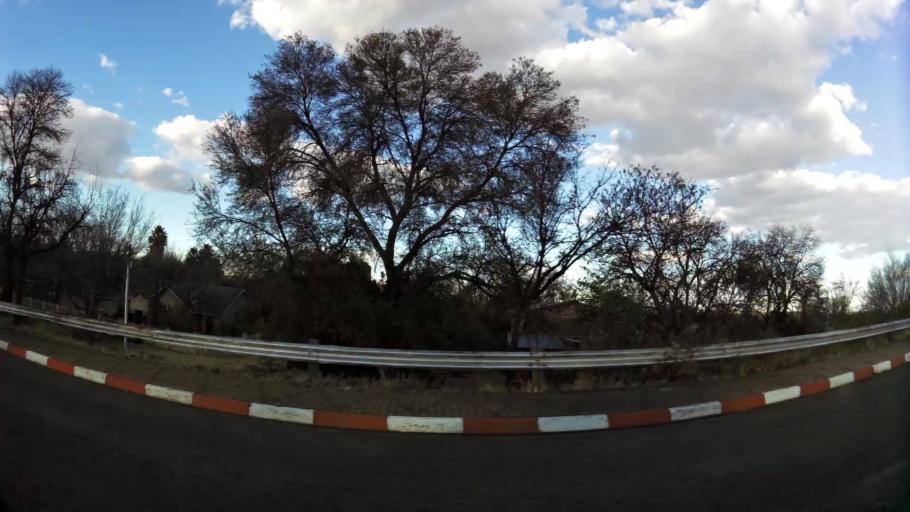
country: ZA
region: North-West
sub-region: Dr Kenneth Kaunda District Municipality
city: Potchefstroom
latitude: -26.6795
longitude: 27.0960
